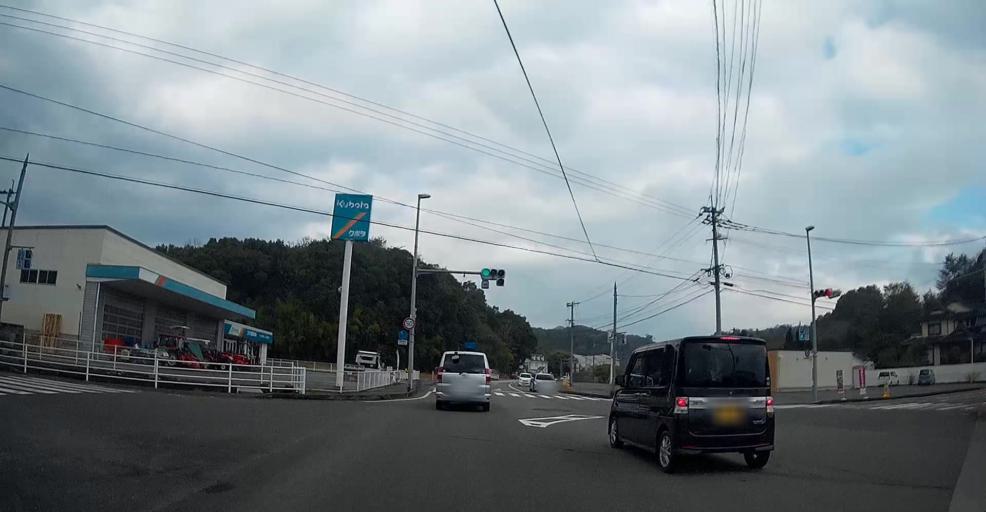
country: JP
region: Kumamoto
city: Yatsushiro
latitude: 32.5524
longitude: 130.4180
